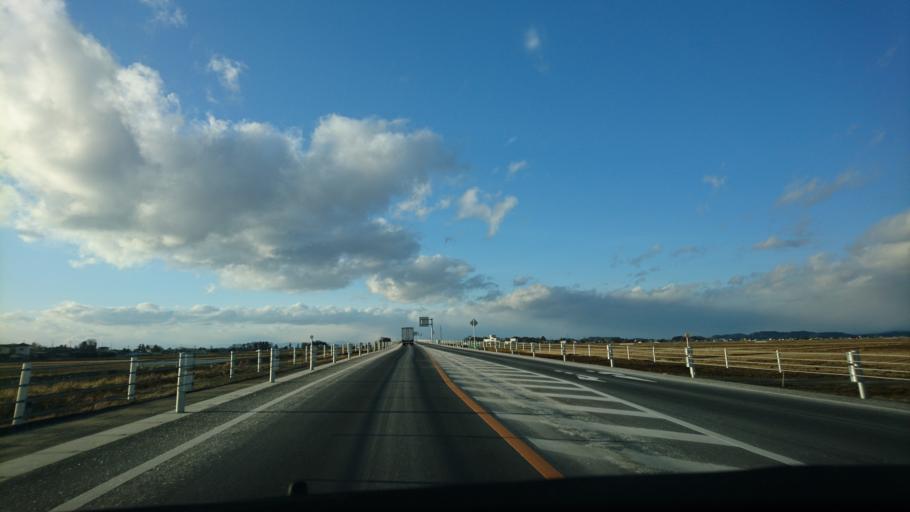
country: JP
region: Miyagi
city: Wakuya
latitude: 38.6783
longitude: 141.2593
